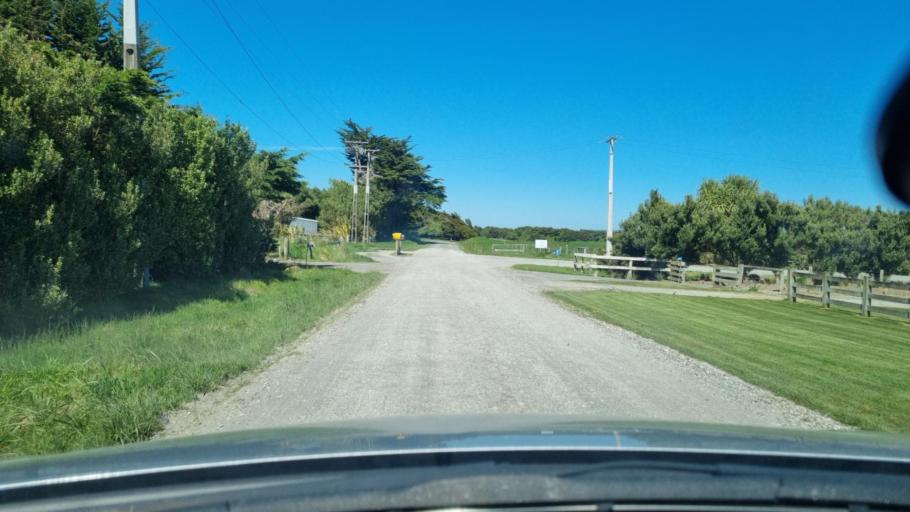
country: NZ
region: Southland
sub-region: Invercargill City
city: Invercargill
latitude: -46.4440
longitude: 168.2784
